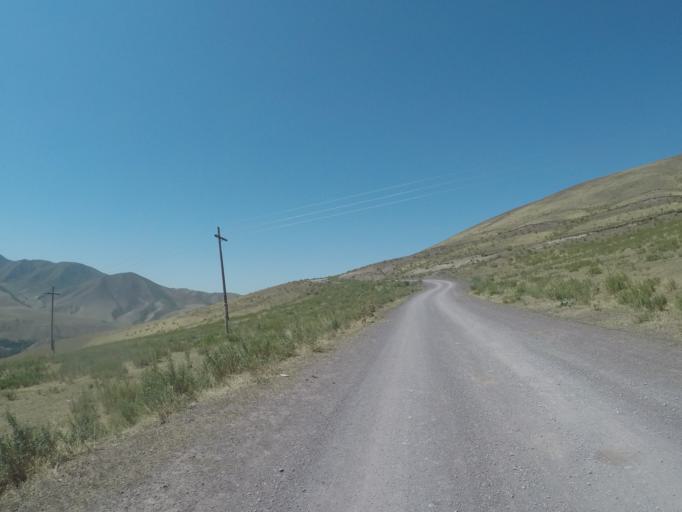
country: KG
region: Chuy
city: Bishkek
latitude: 42.6500
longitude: 74.5171
